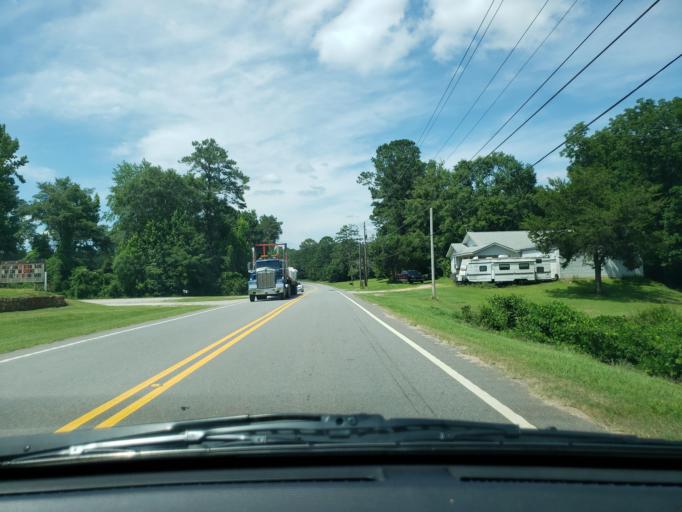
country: US
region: Alabama
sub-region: Elmore County
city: Eclectic
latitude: 32.6775
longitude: -85.9442
